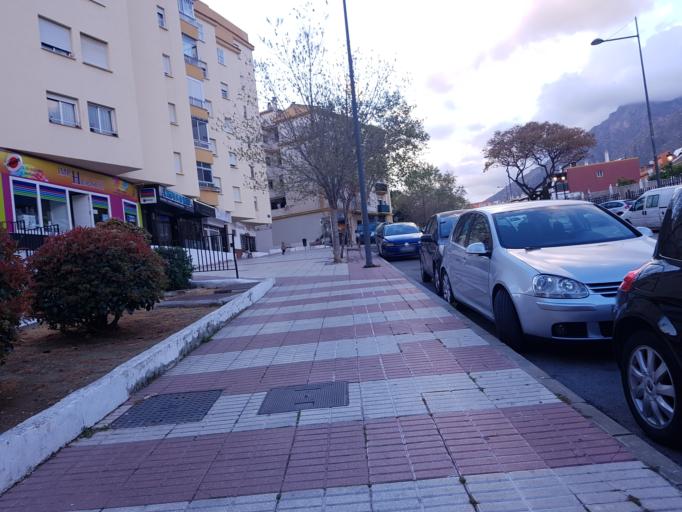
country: ES
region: Andalusia
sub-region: Provincia de Malaga
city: Marbella
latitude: 36.5172
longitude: -4.8877
